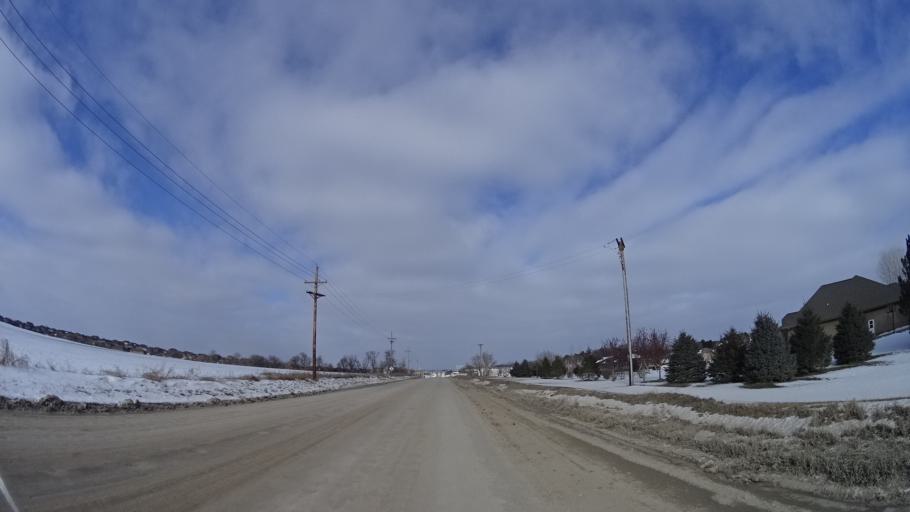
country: US
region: Nebraska
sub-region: Sarpy County
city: Papillion
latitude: 41.1187
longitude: -96.0237
